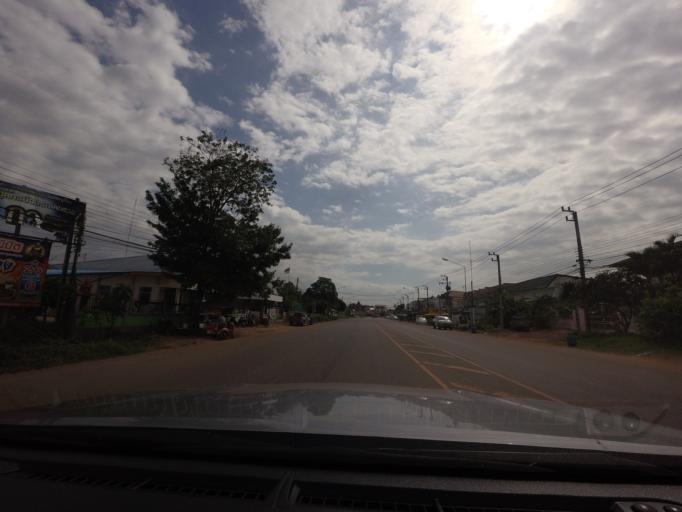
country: TH
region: Phitsanulok
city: Noen Maprang
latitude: 16.5693
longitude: 100.6343
